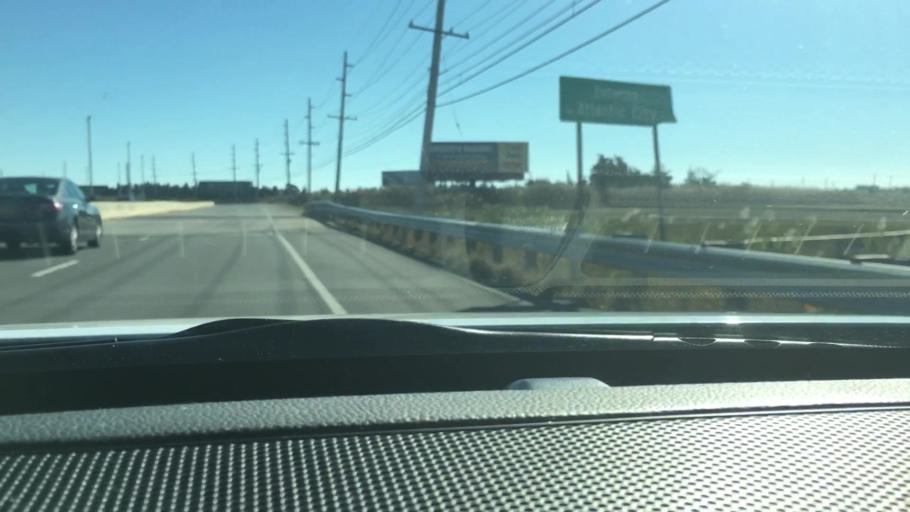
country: US
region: New Jersey
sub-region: Atlantic County
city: Pleasantville
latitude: 39.3899
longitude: -74.4987
